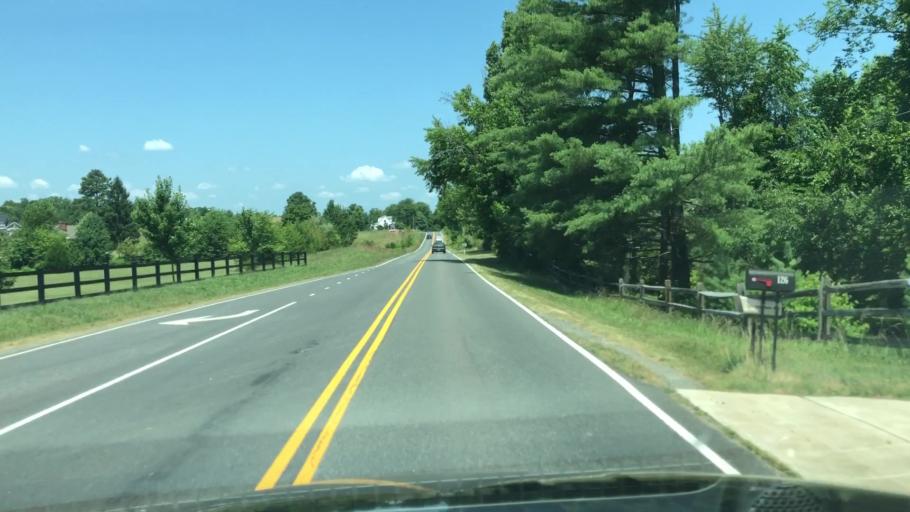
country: US
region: Virginia
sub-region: Stafford County
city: Falmouth
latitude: 38.4095
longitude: -77.5674
